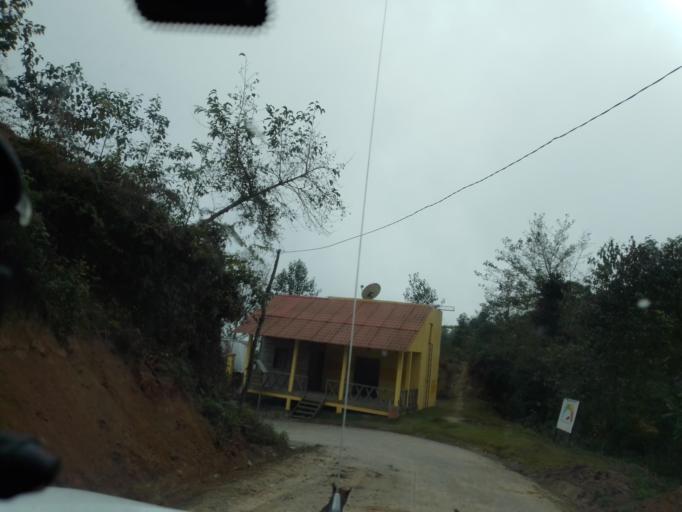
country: MX
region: Chiapas
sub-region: Union Juarez
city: Santo Domingo
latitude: 15.0926
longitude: -92.0997
